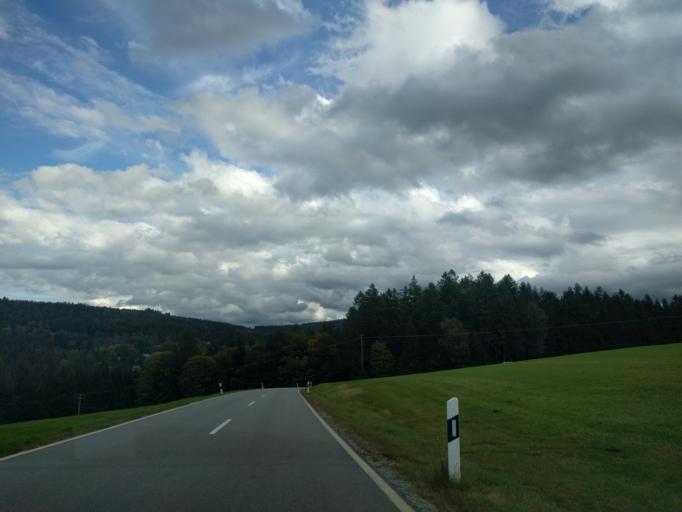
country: DE
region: Bavaria
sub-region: Lower Bavaria
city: Schaufling
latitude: 48.8729
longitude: 13.0291
